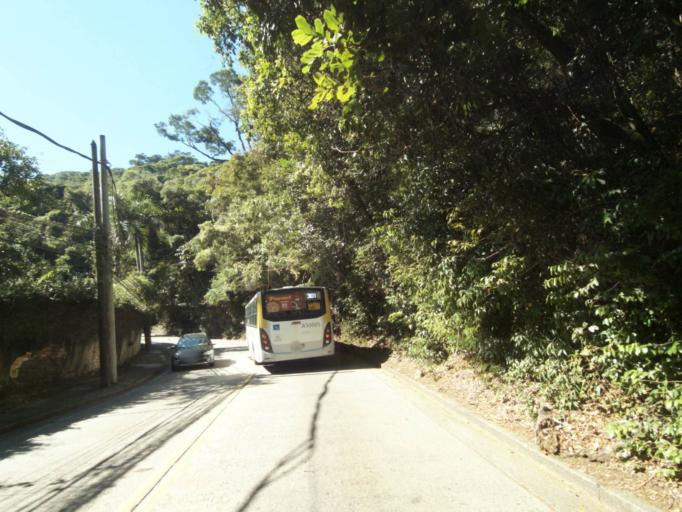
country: BR
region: Rio de Janeiro
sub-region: Rio De Janeiro
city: Rio de Janeiro
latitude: -22.9699
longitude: -43.2796
